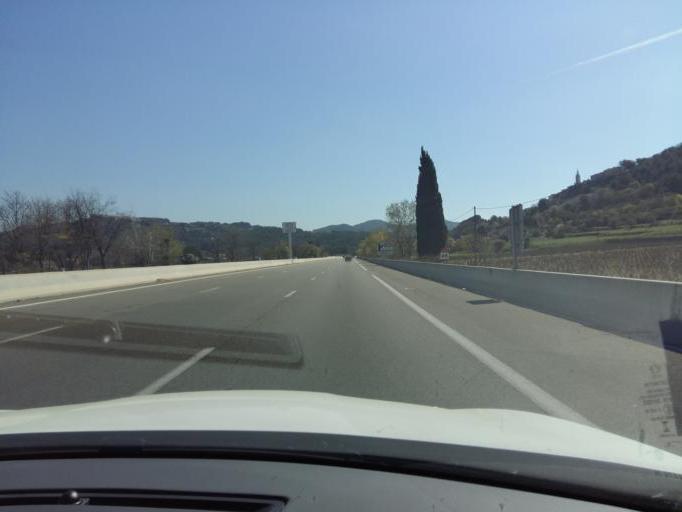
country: FR
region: Provence-Alpes-Cote d'Azur
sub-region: Departement du Var
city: Le Castellet
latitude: 43.2017
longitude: 5.7489
